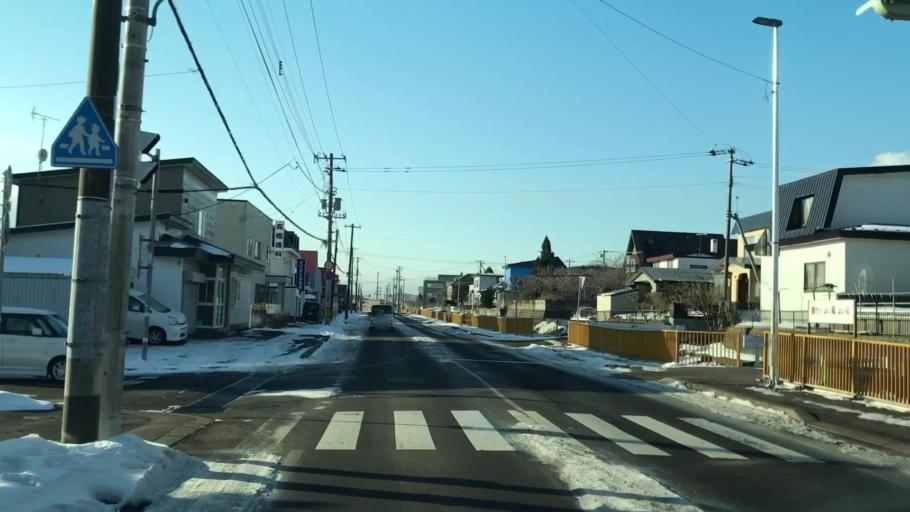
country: JP
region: Hokkaido
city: Muroran
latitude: 42.3685
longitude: 141.0504
